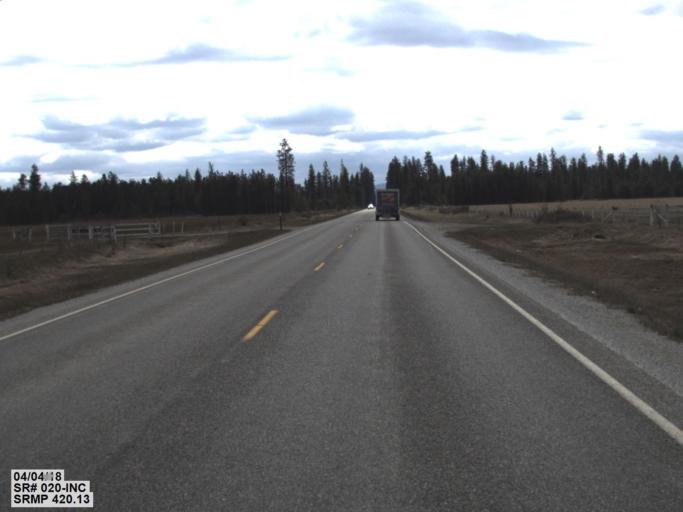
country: US
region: Washington
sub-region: Pend Oreille County
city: Newport
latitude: 48.3227
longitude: -117.2957
